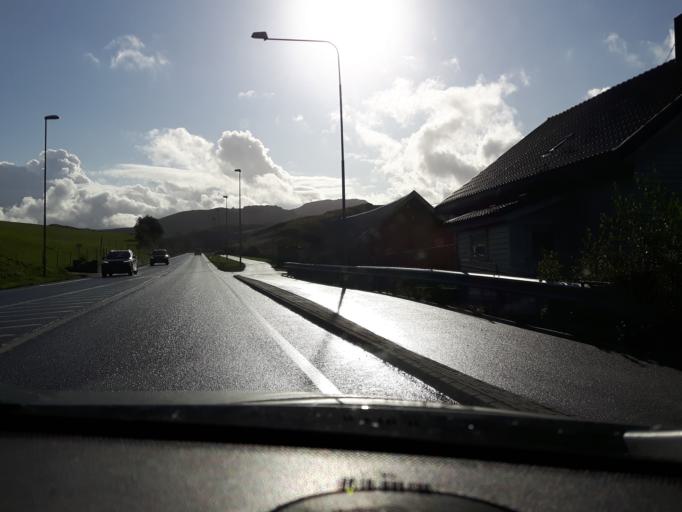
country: NO
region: Rogaland
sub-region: Gjesdal
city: Algard
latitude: 58.7652
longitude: 5.8866
